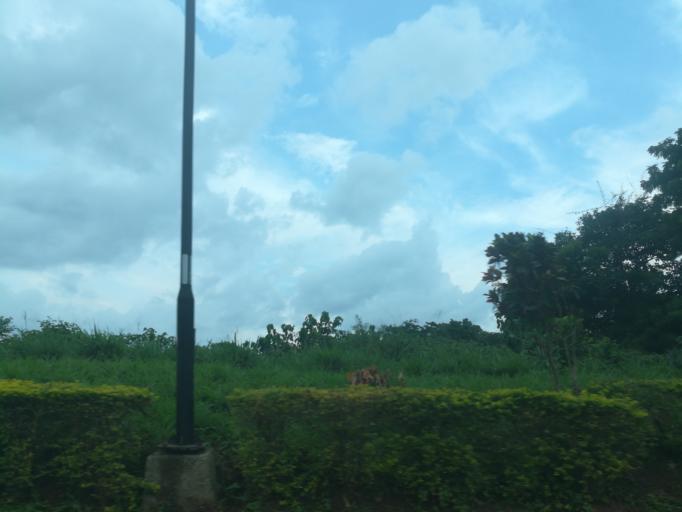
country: NG
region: Lagos
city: Ikorodu
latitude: 6.6390
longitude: 3.5212
